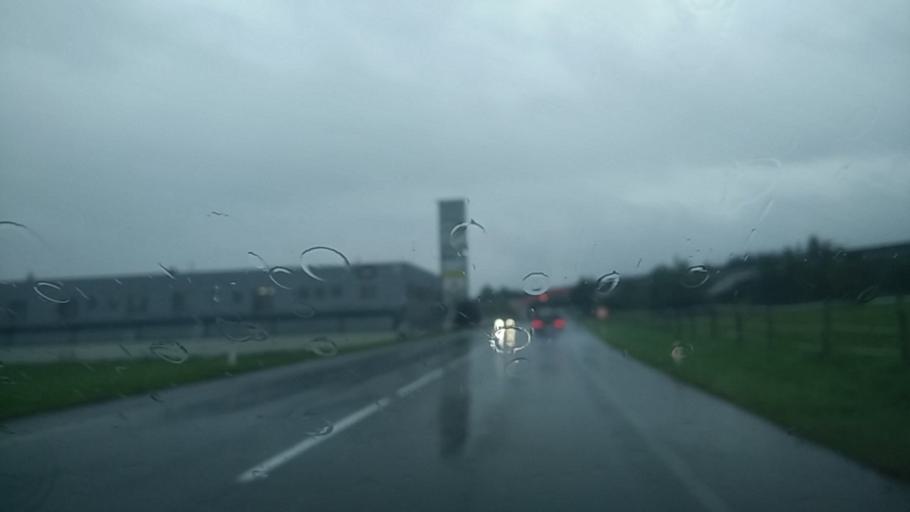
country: AT
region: Carinthia
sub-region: Politischer Bezirk Villach Land
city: Wernberg
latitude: 46.6205
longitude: 13.9459
